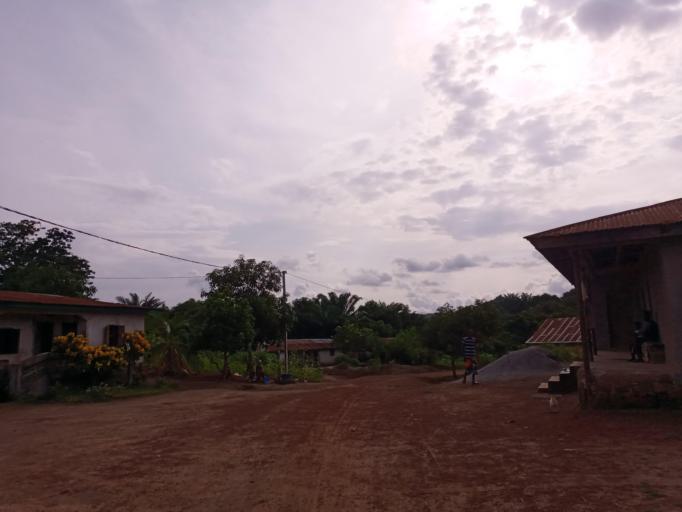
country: SL
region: Northern Province
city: Bumbuna
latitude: 9.0499
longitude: -11.7561
